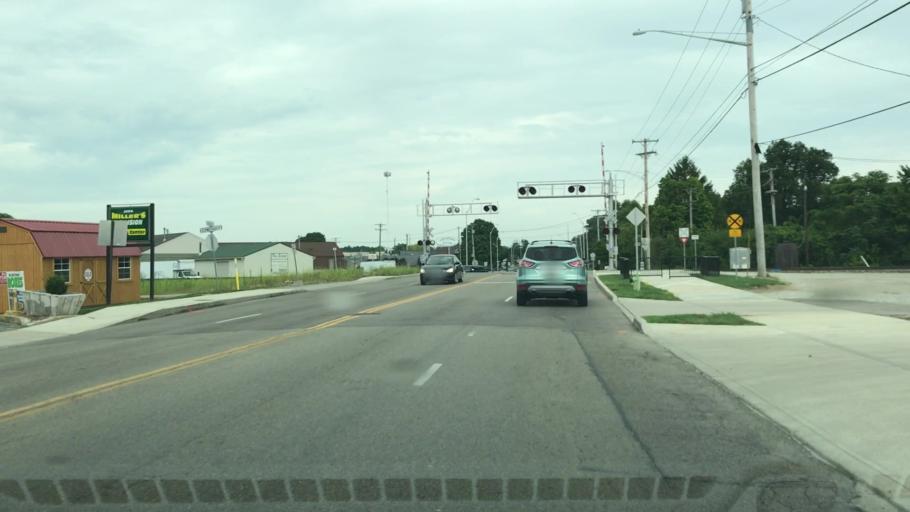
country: US
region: Ohio
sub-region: Greene County
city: Fairborn
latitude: 39.8221
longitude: -84.0142
